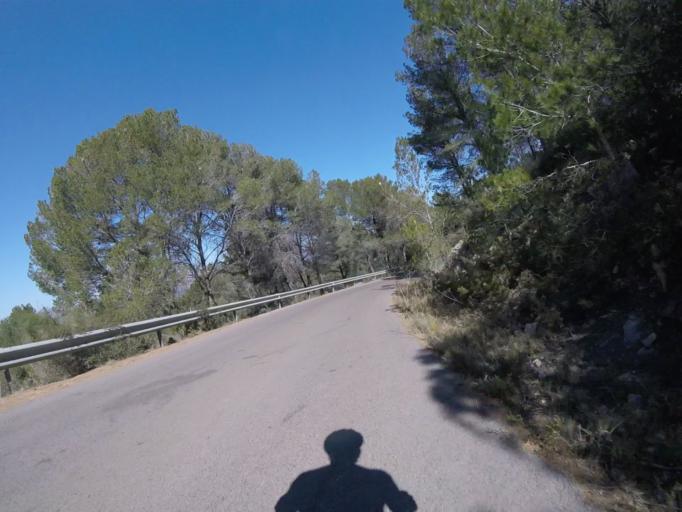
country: ES
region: Valencia
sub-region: Provincia de Castello
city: Cervera del Maestre
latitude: 40.4088
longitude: 0.1948
